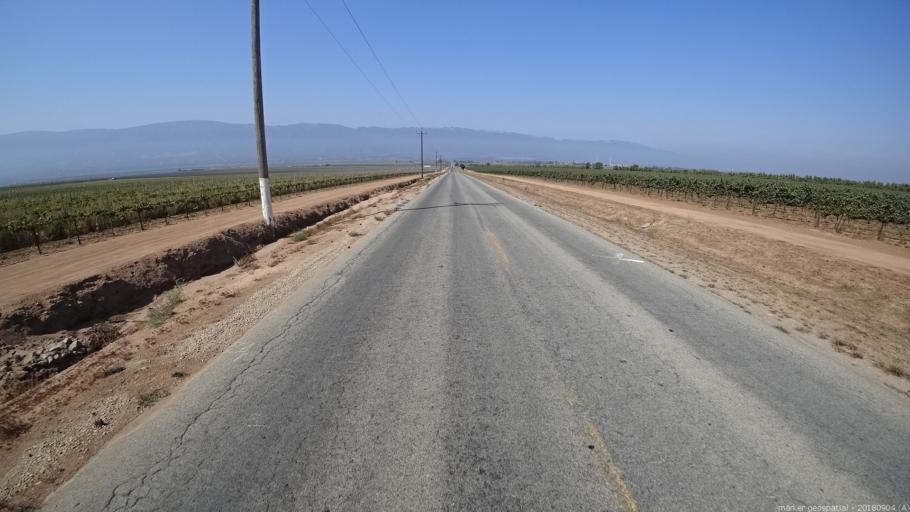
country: US
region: California
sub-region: Monterey County
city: Gonzales
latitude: 36.4995
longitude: -121.4042
